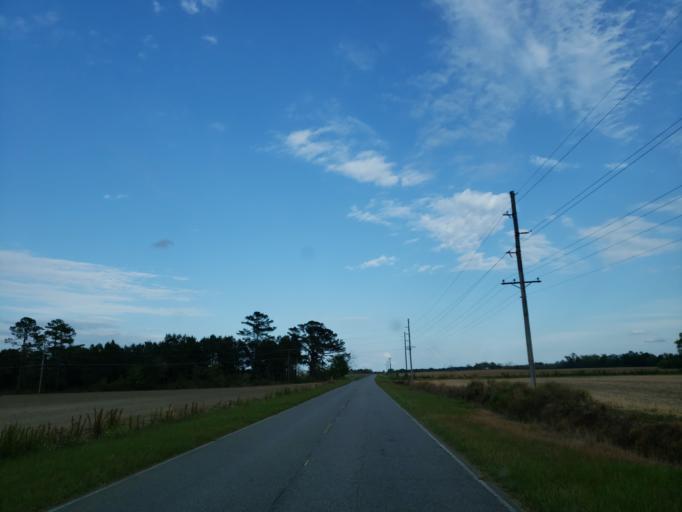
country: US
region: Georgia
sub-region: Dooly County
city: Vienna
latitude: 32.1236
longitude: -83.7073
